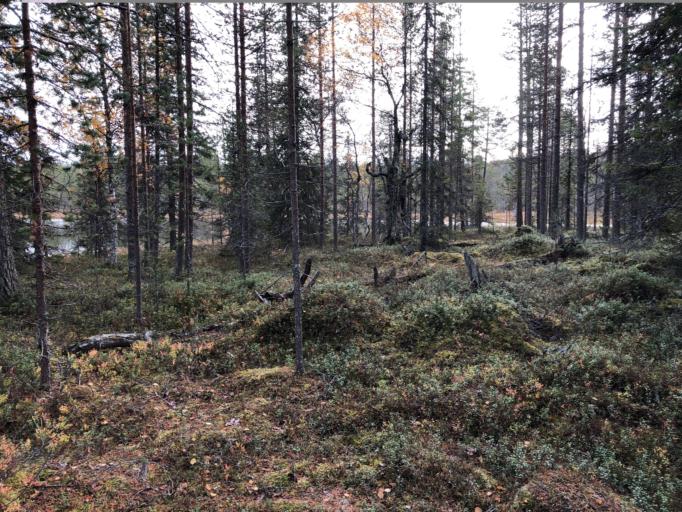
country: FI
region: Lapland
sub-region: Itae-Lappi
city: Posio
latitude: 66.3280
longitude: 28.4385
